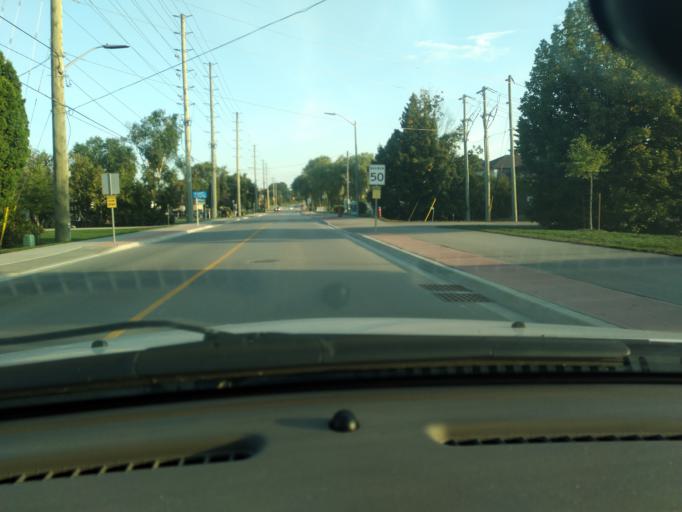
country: CA
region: Ontario
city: Bradford West Gwillimbury
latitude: 44.0979
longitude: -79.5684
